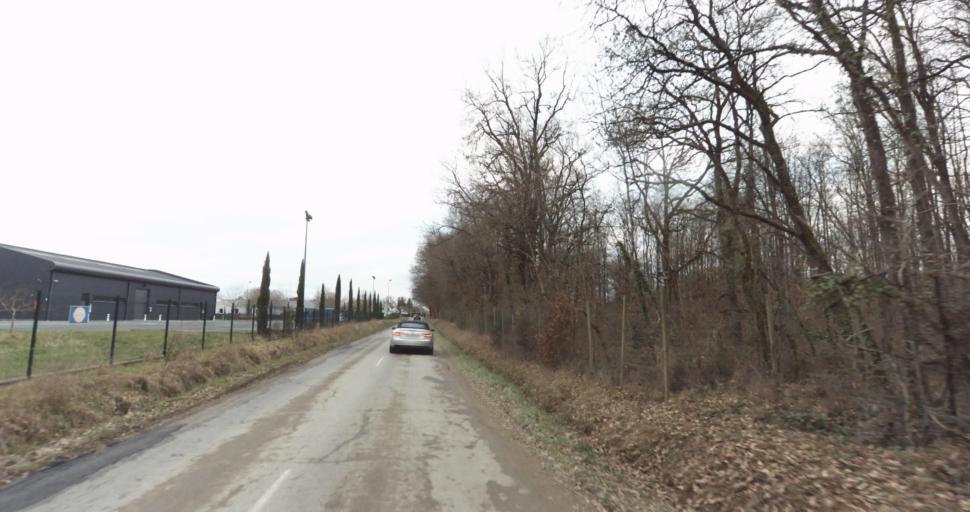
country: FR
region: Pays de la Loire
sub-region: Departement de Maine-et-Loire
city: Distre
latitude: 47.2537
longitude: -0.1135
